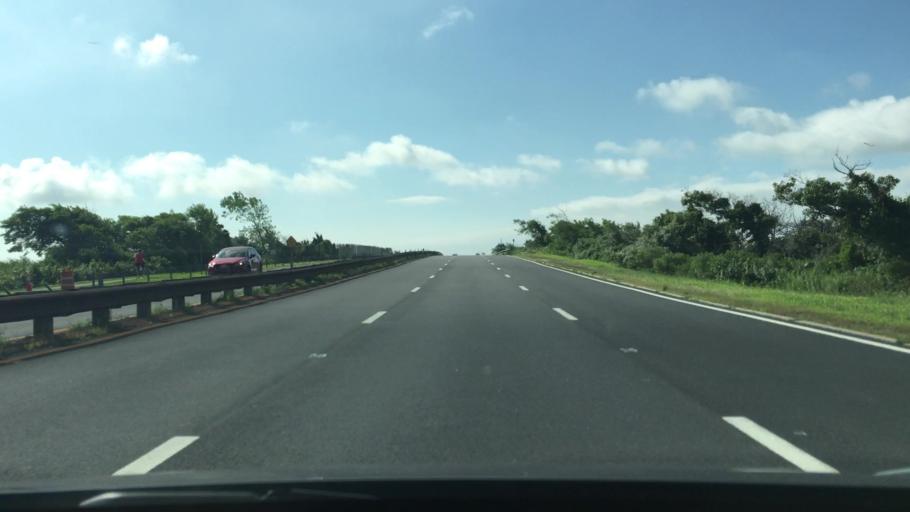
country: US
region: New York
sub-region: Nassau County
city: Seaford
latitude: 40.6414
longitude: -73.5087
